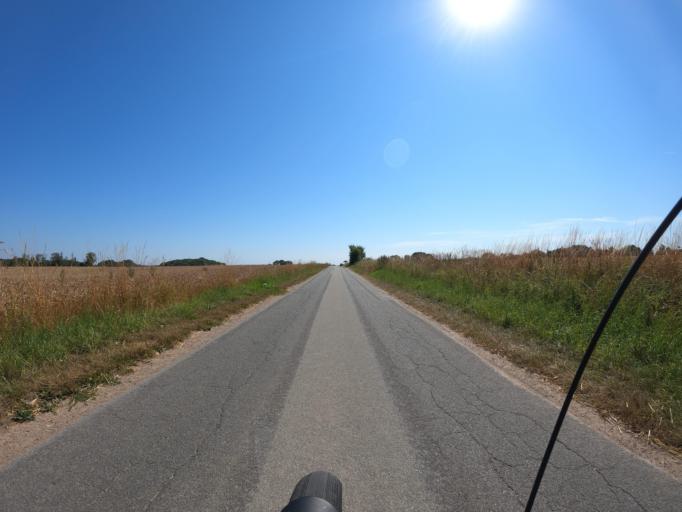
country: DE
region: Schleswig-Holstein
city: Steinberg
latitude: 54.7692
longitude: 9.7698
